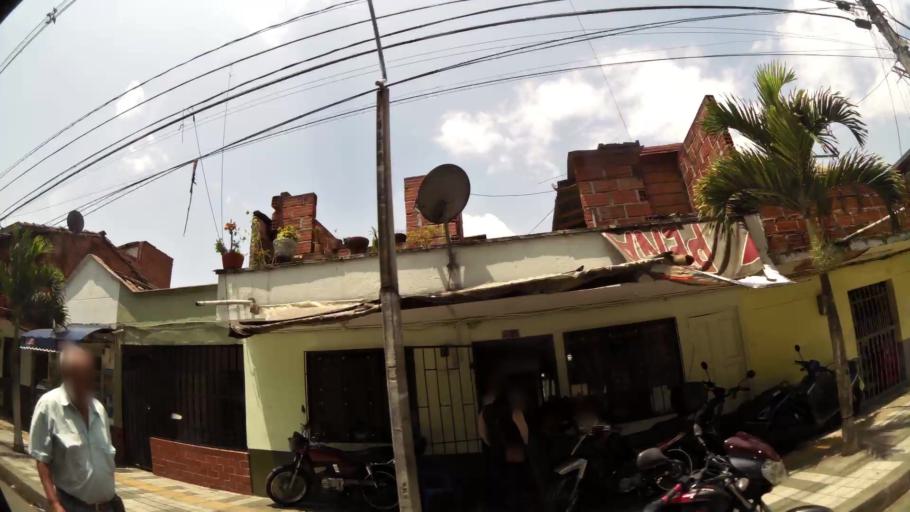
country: CO
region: Antioquia
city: Itagui
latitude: 6.1752
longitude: -75.6120
